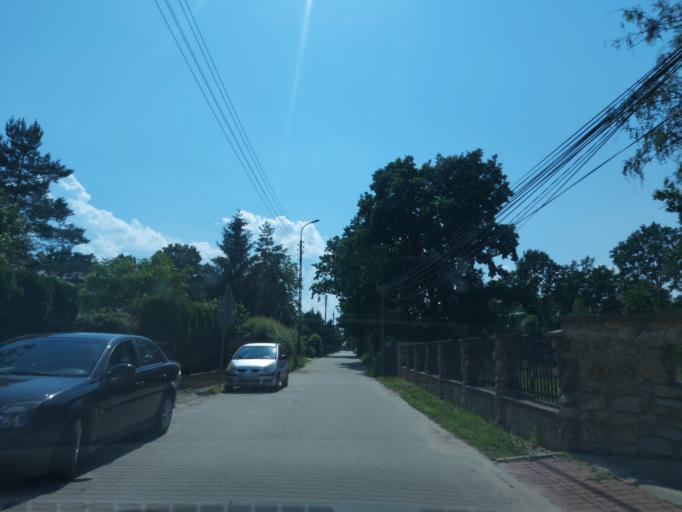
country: PL
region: Masovian Voivodeship
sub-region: Powiat piaseczynski
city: Piaseczno
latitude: 52.0626
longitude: 20.9826
